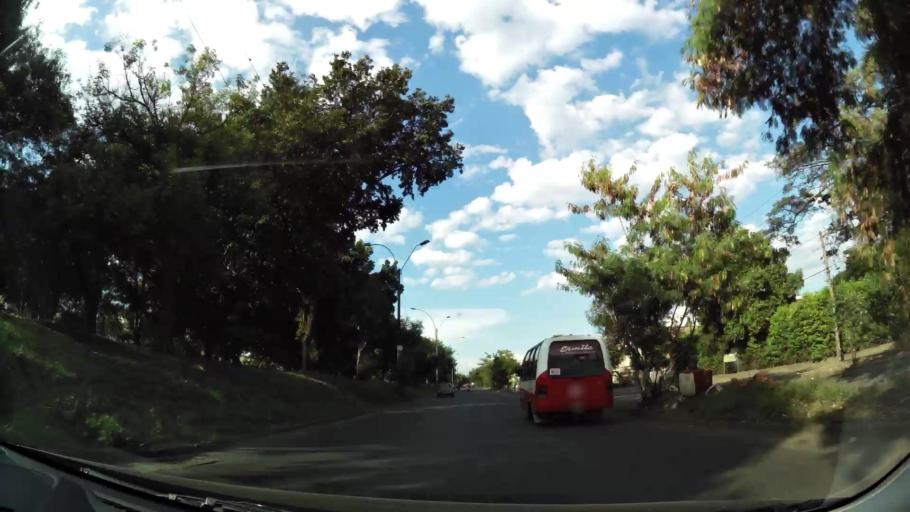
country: CO
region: Valle del Cauca
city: Cali
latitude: 3.4355
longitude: -76.4949
